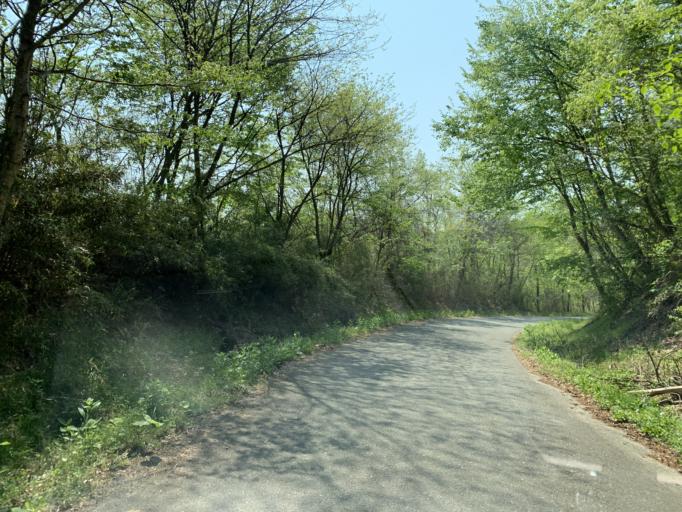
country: JP
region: Iwate
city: Ichinoseki
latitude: 38.8887
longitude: 141.0589
